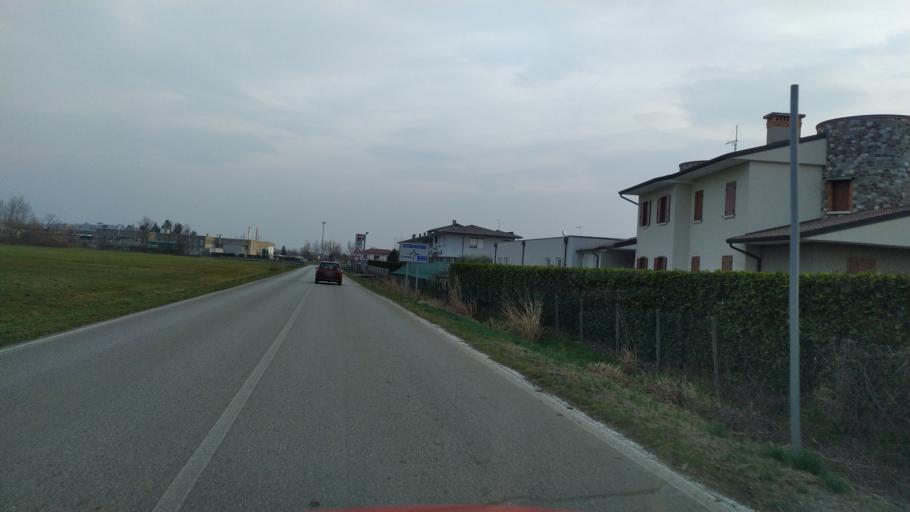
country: IT
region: Veneto
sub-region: Provincia di Vicenza
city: Preara-Moraro-Leva Nord
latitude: 45.6872
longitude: 11.5321
